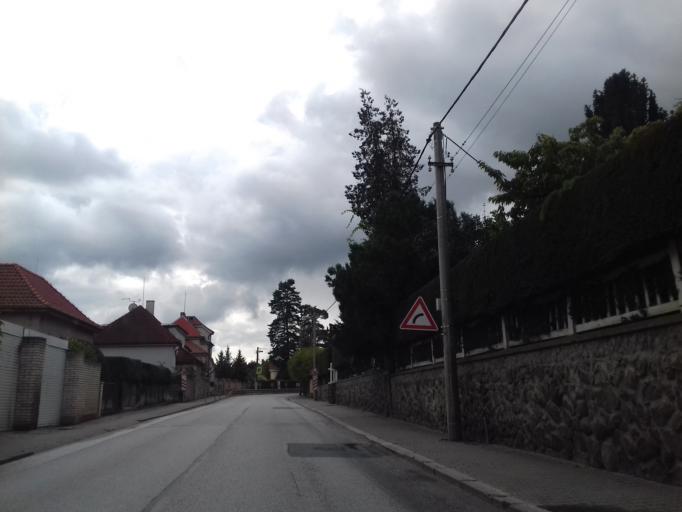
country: CZ
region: Central Bohemia
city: Cernosice
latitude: 49.9618
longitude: 14.3256
